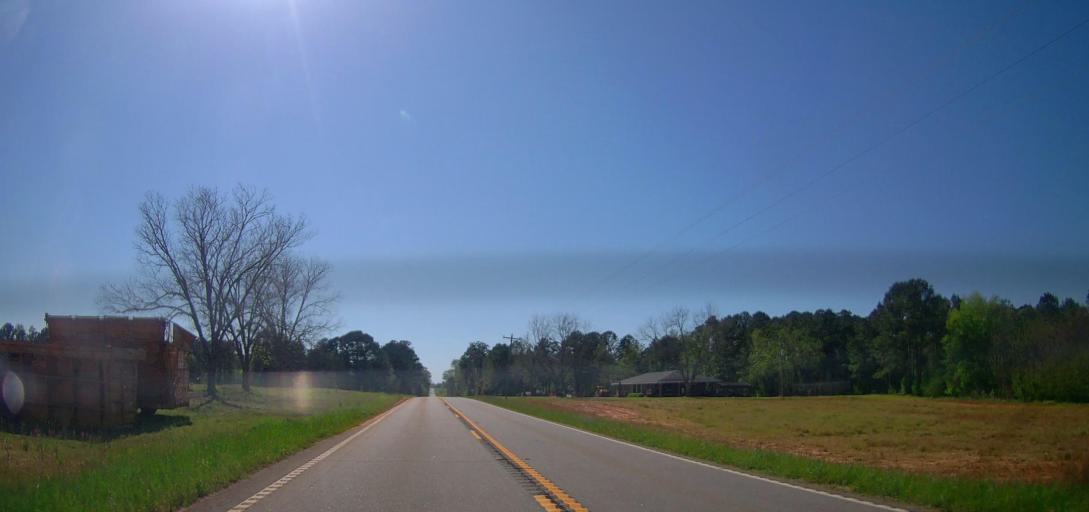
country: US
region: Georgia
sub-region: Dooly County
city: Unadilla
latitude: 32.2600
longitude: -83.6783
